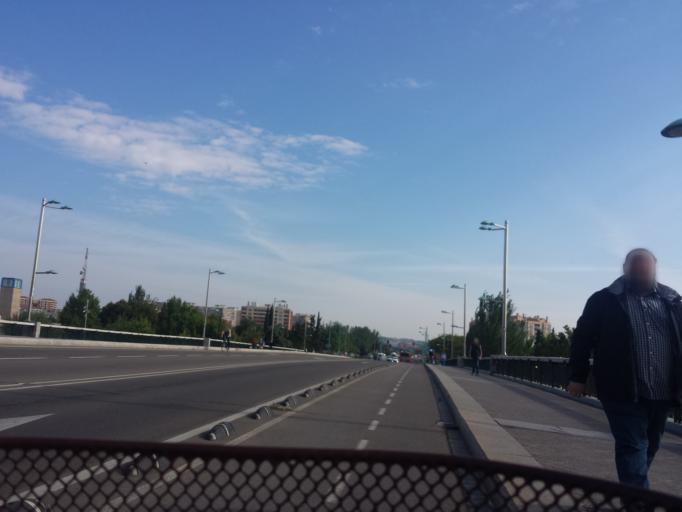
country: ES
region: Aragon
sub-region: Provincia de Zaragoza
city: Zaragoza
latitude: 41.6583
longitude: -0.8815
